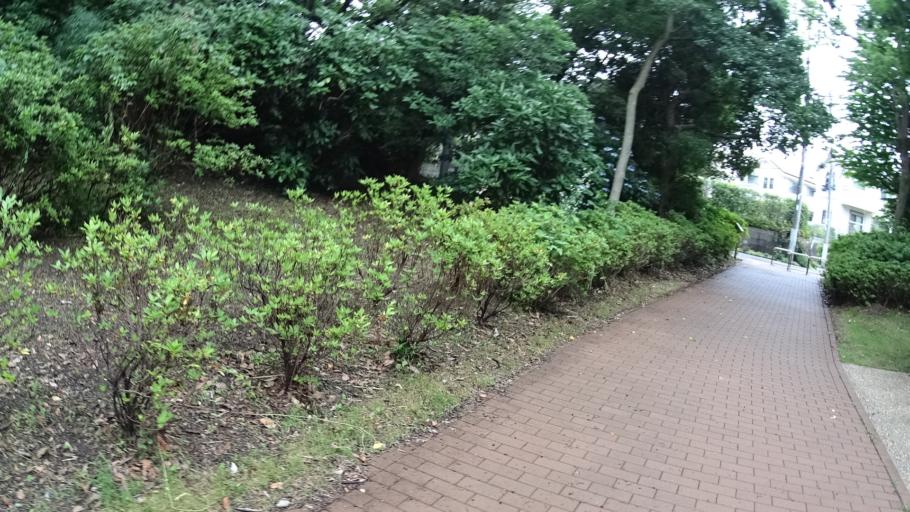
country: JP
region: Kanagawa
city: Zushi
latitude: 35.3517
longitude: 139.6178
